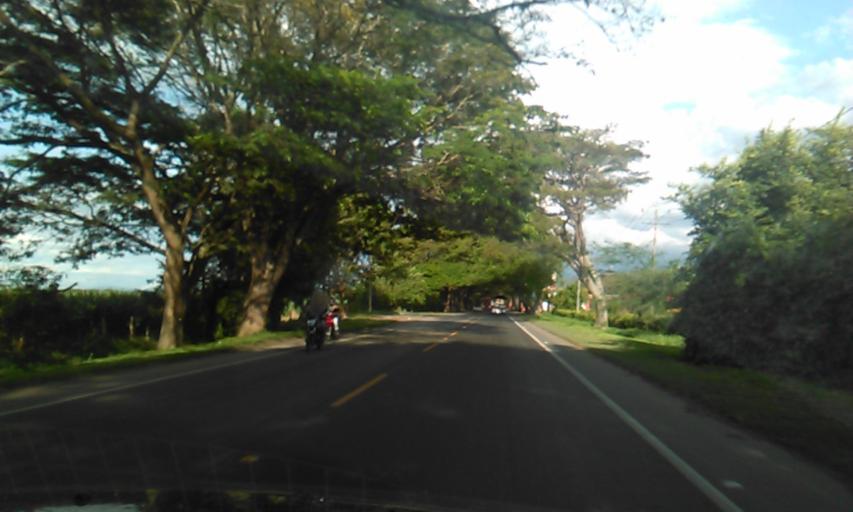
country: CO
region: Valle del Cauca
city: Buga
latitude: 3.8912
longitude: -76.3206
